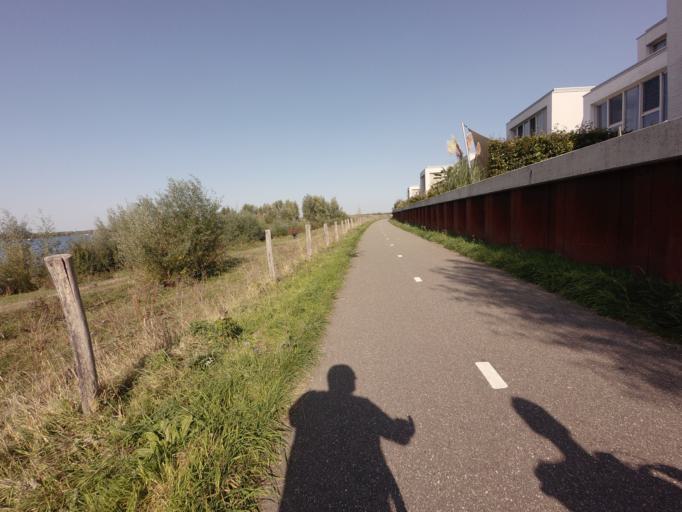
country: NL
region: Limburg
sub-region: Gemeente Roermond
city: Roermond
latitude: 51.1760
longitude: 5.9527
